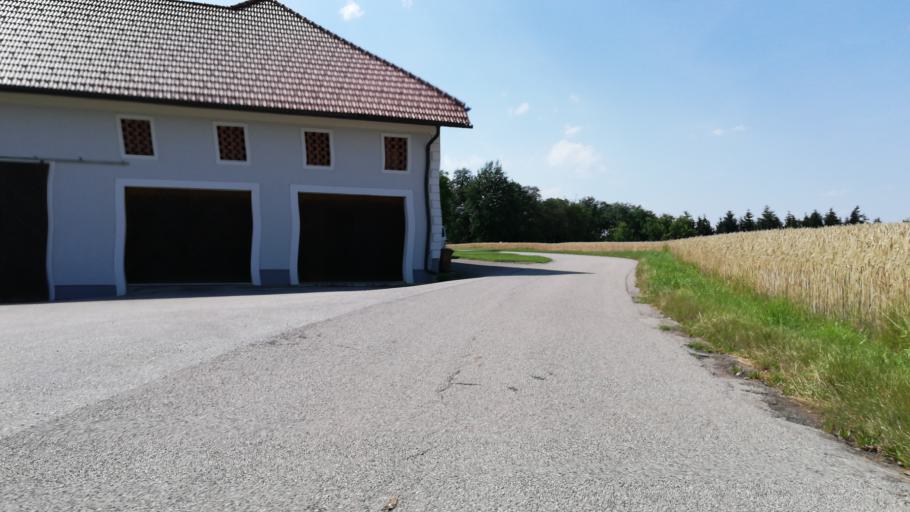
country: AT
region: Upper Austria
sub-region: Wels-Land
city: Edt bei Lambach
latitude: 48.1684
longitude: 13.8955
